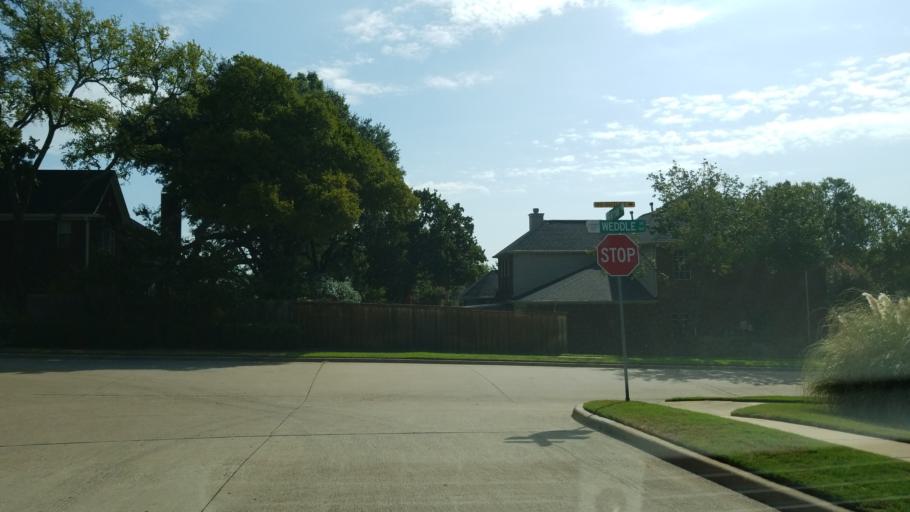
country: US
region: Texas
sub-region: Tarrant County
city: Grapevine
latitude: 32.8897
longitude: -97.0907
